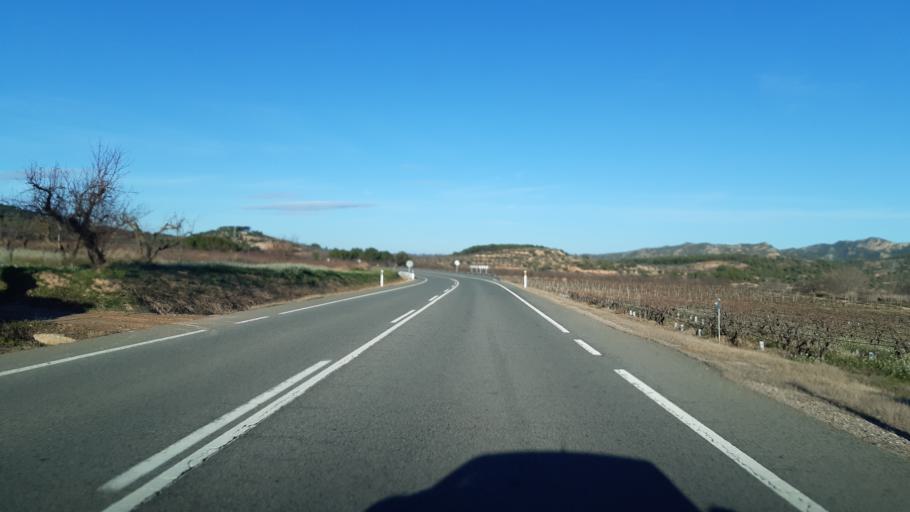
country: ES
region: Catalonia
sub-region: Provincia de Tarragona
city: la Fatarella
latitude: 41.0908
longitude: 0.5140
